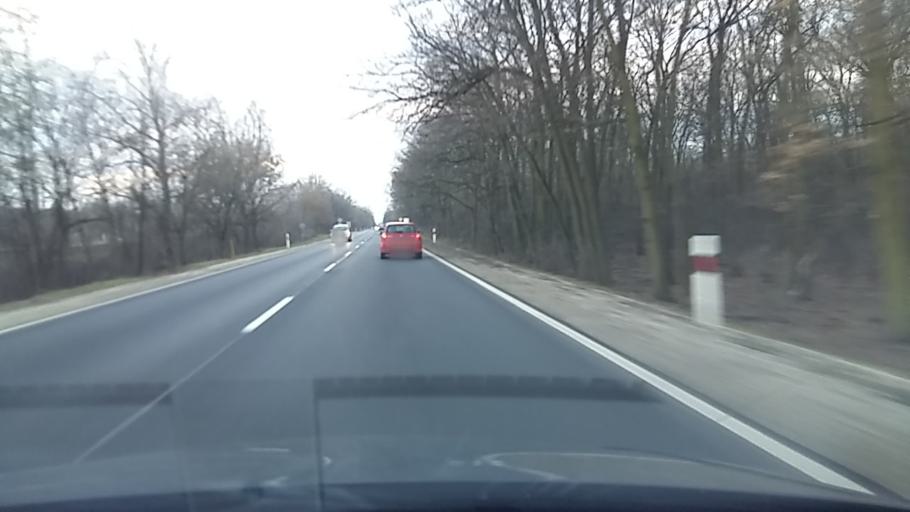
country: HU
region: Hajdu-Bihar
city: Debrecen
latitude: 47.5698
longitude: 21.6527
